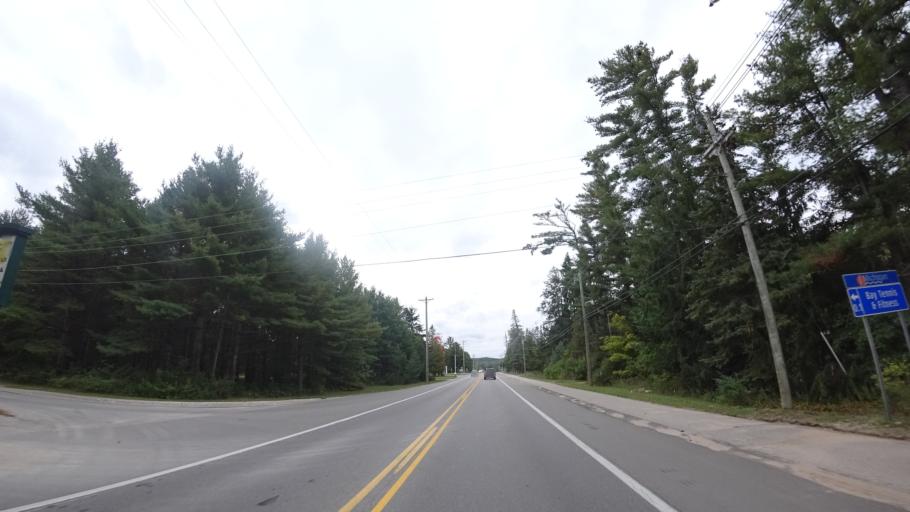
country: US
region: Michigan
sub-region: Emmet County
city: Petoskey
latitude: 45.4235
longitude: -84.9045
